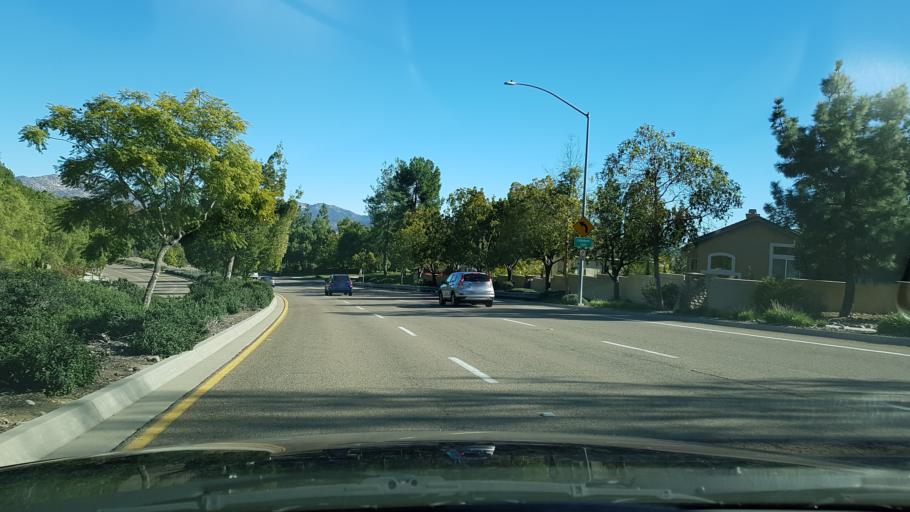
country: US
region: California
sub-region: San Diego County
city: Poway
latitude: 32.9711
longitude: -117.0731
